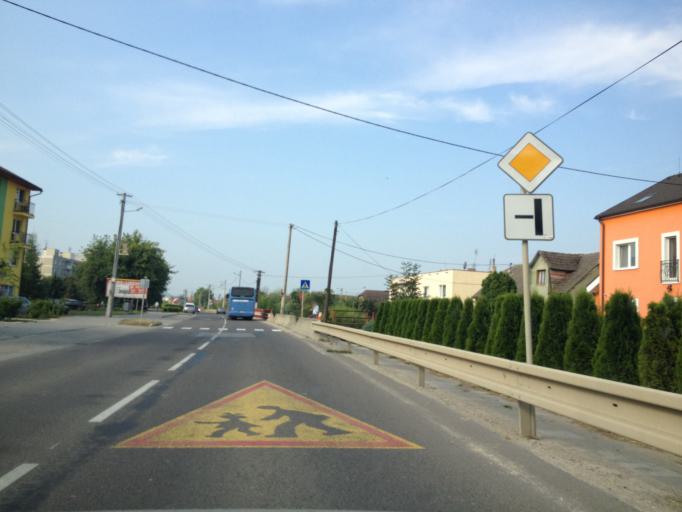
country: SK
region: Nitriansky
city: Puchov
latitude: 49.0644
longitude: 18.3256
